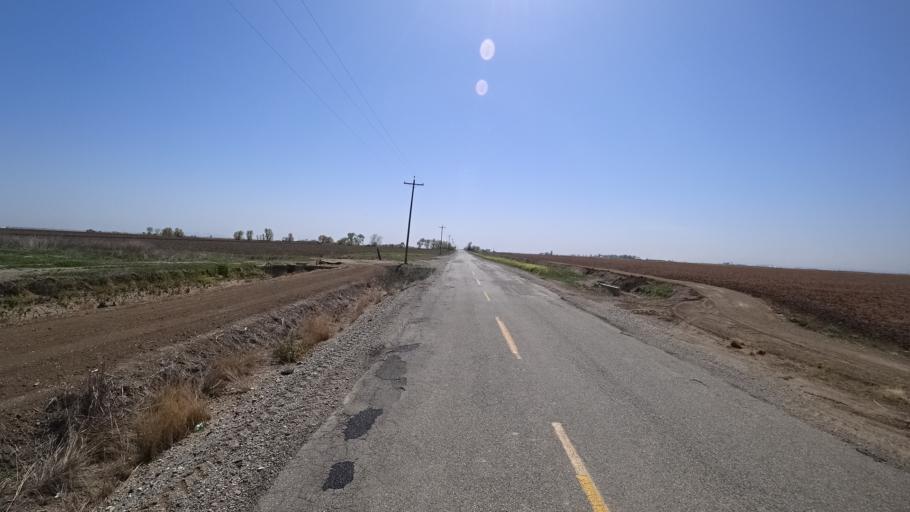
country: US
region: California
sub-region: Glenn County
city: Willows
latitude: 39.5091
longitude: -122.1368
